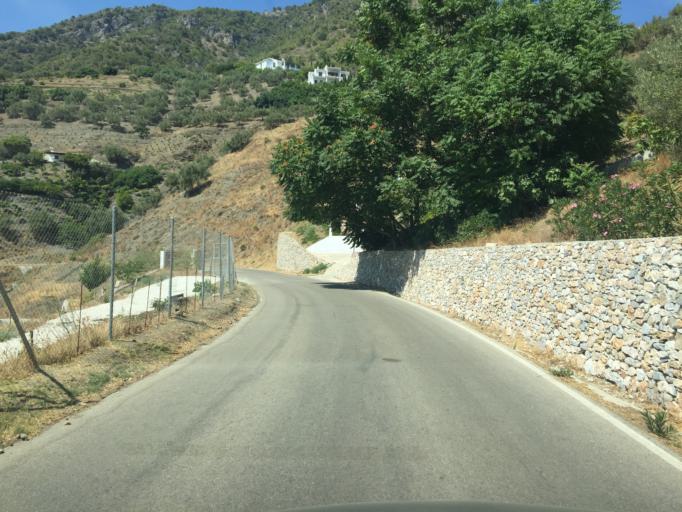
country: ES
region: Andalusia
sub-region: Provincia de Malaga
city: Frigiliana
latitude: 36.8036
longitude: -3.9194
